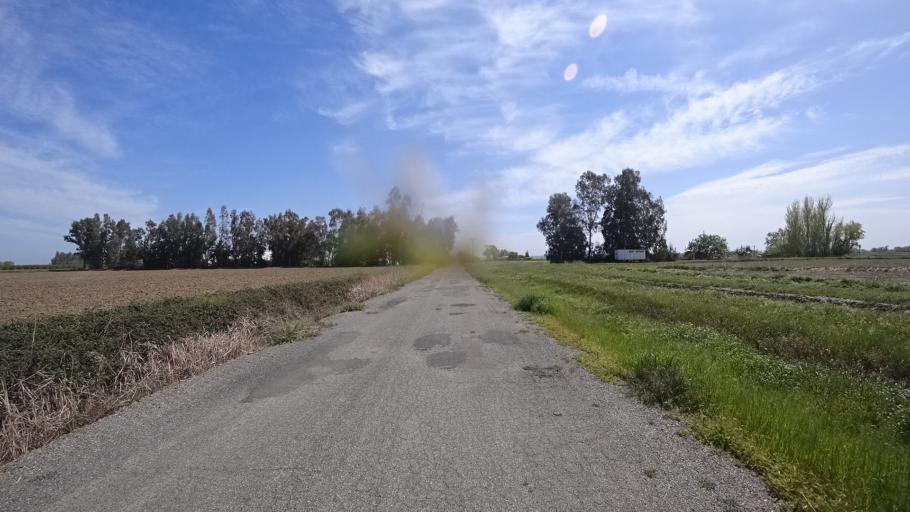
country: US
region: California
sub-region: Glenn County
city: Willows
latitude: 39.5948
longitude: -122.0622
